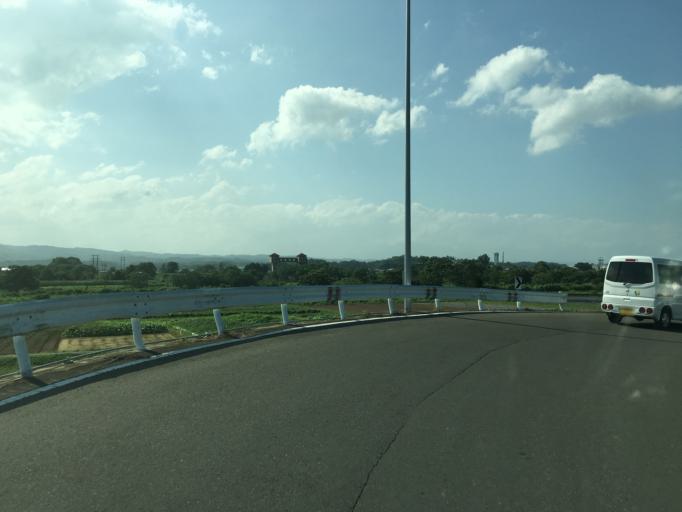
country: JP
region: Miyagi
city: Kakuda
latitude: 37.9600
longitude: 140.7897
